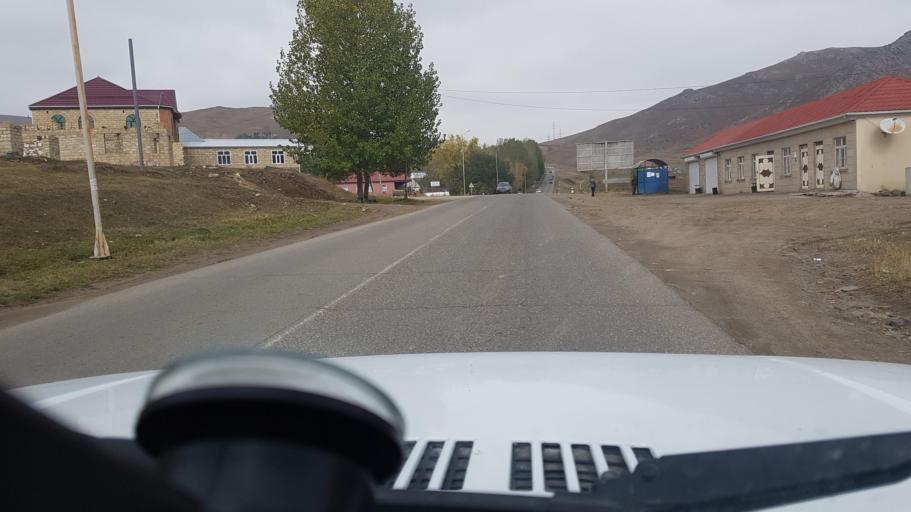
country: AZ
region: Gadabay Rayon
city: Ariqdam
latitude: 40.6061
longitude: 45.8124
